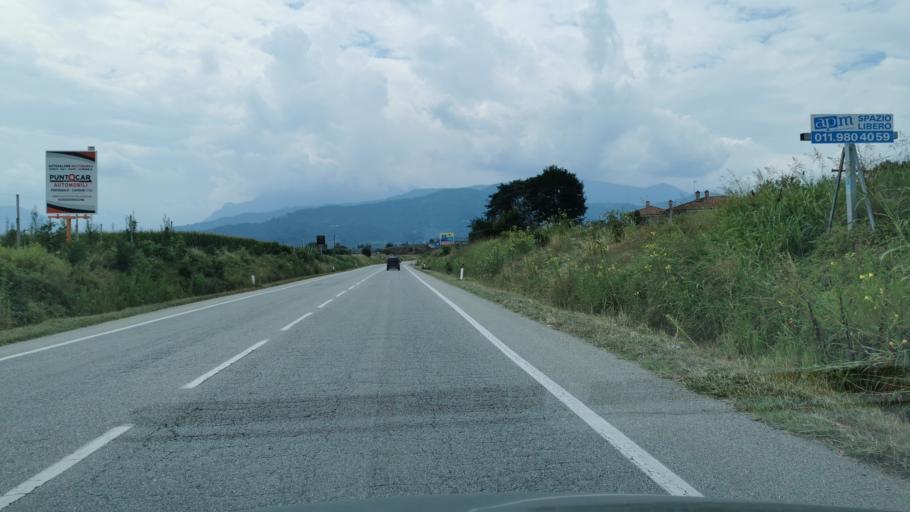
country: IT
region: Piedmont
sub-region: Provincia di Torino
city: Osasco
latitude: 44.8446
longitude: 7.3424
